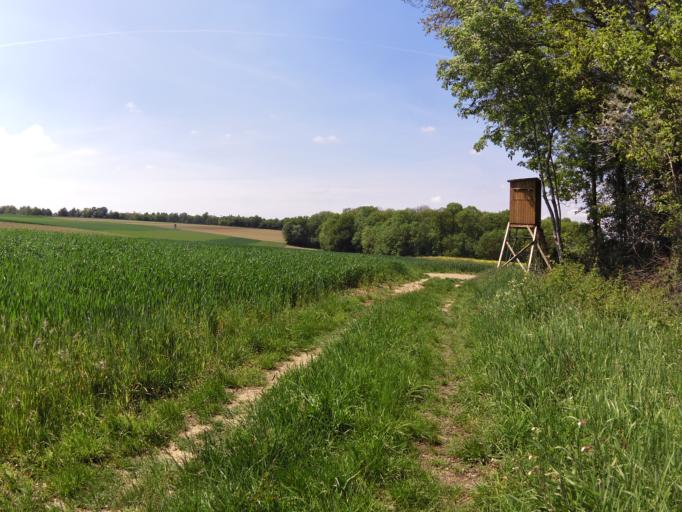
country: DE
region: Bavaria
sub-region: Regierungsbezirk Unterfranken
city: Theilheim
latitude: 49.7423
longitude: 10.0234
